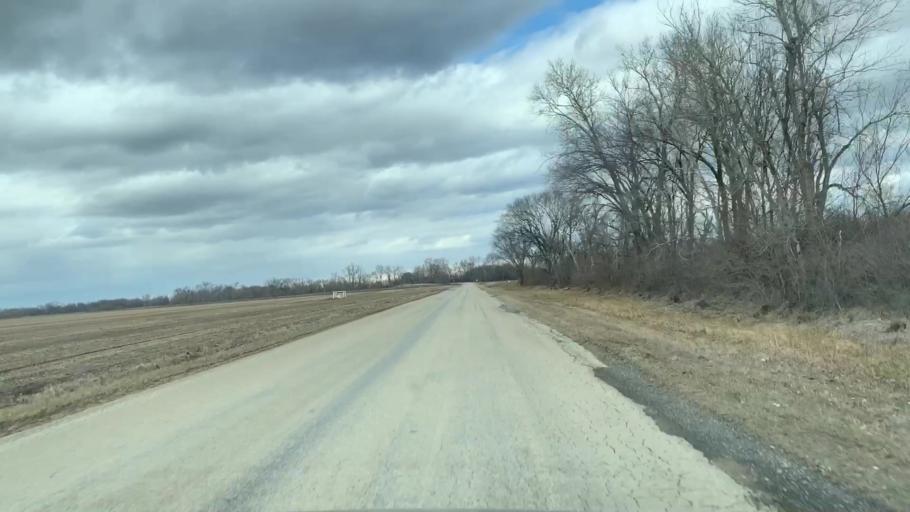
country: US
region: Kansas
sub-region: Allen County
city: Humboldt
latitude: 37.7967
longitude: -95.4706
